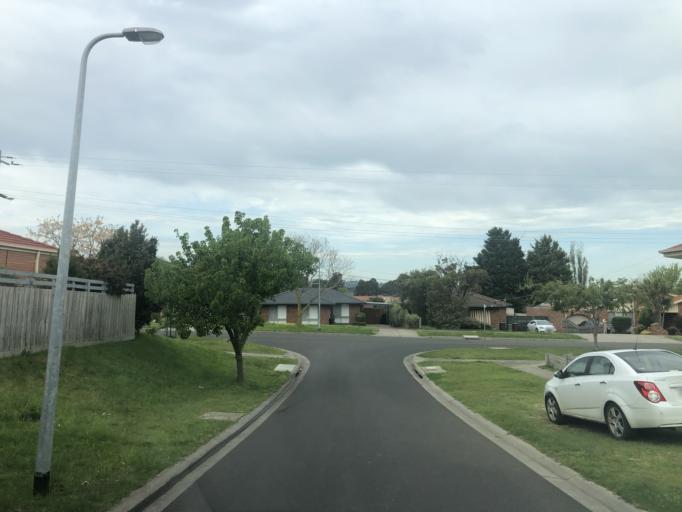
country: AU
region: Victoria
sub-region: Casey
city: Hallam
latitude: -38.0028
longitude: 145.2798
